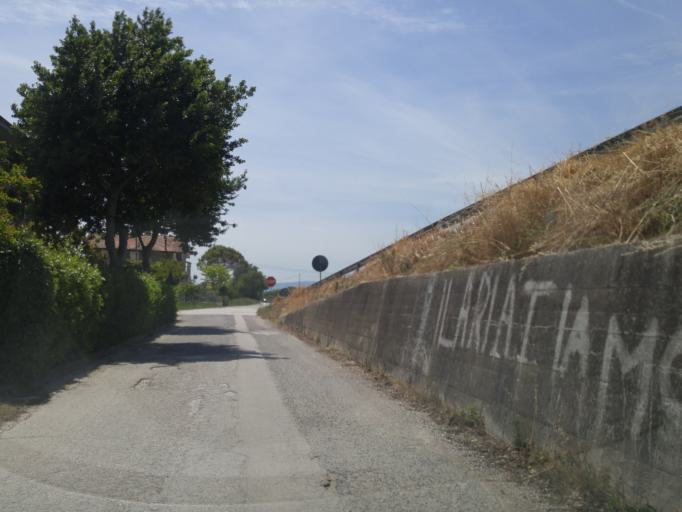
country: IT
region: The Marches
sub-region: Provincia di Pesaro e Urbino
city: Cuccurano
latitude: 43.7769
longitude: 12.9807
